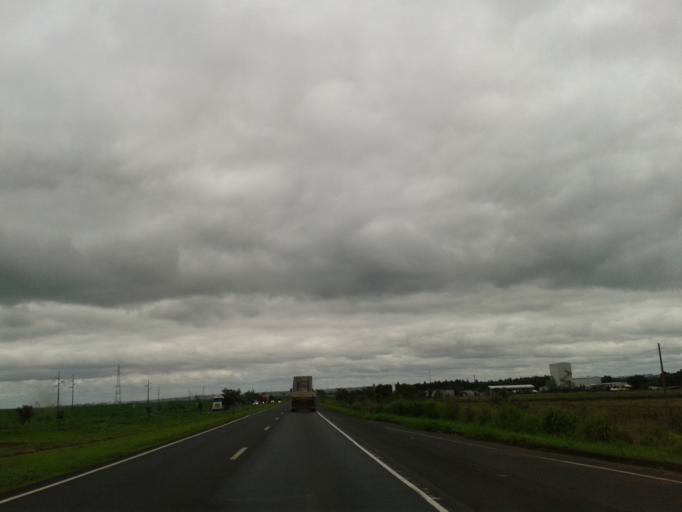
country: BR
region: Minas Gerais
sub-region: Uberlandia
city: Uberlandia
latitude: -19.0437
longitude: -48.1983
